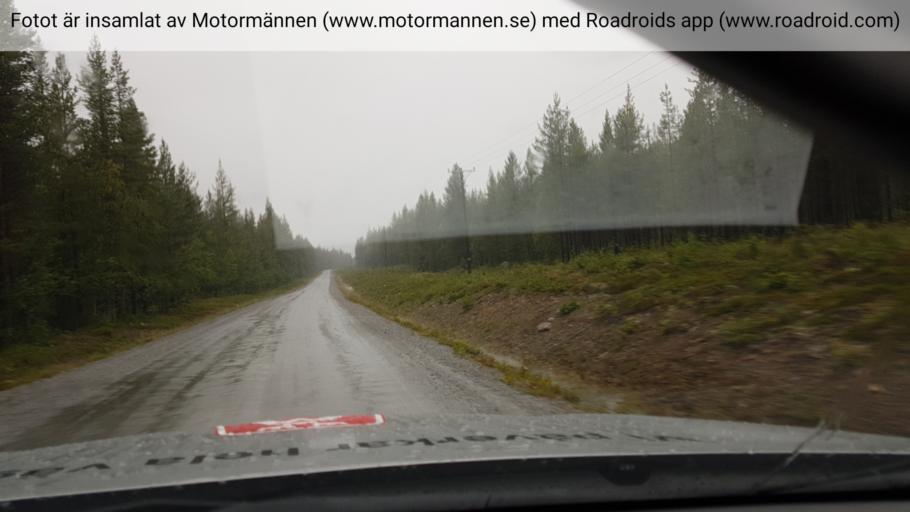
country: SE
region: Norrbotten
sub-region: Jokkmokks Kommun
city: Jokkmokk
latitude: 66.6205
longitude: 18.9261
